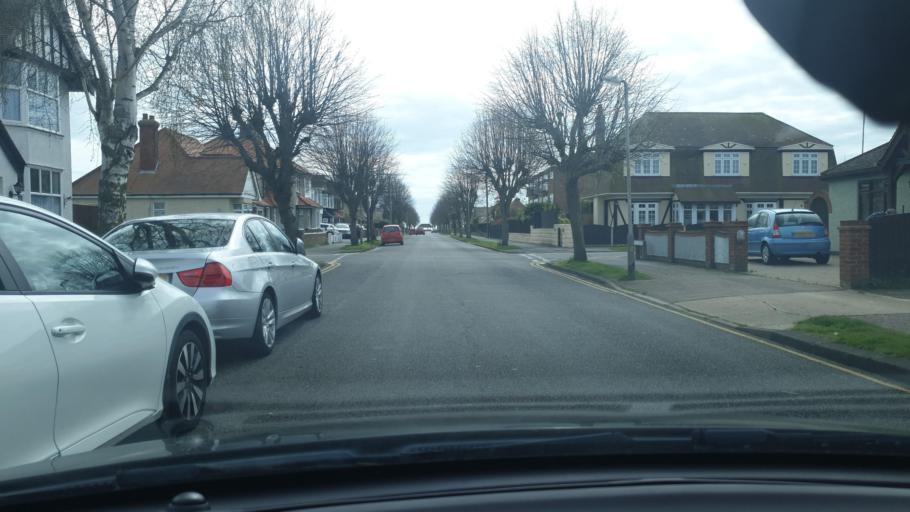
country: GB
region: England
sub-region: Essex
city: Clacton-on-Sea
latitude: 51.8015
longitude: 1.1823
